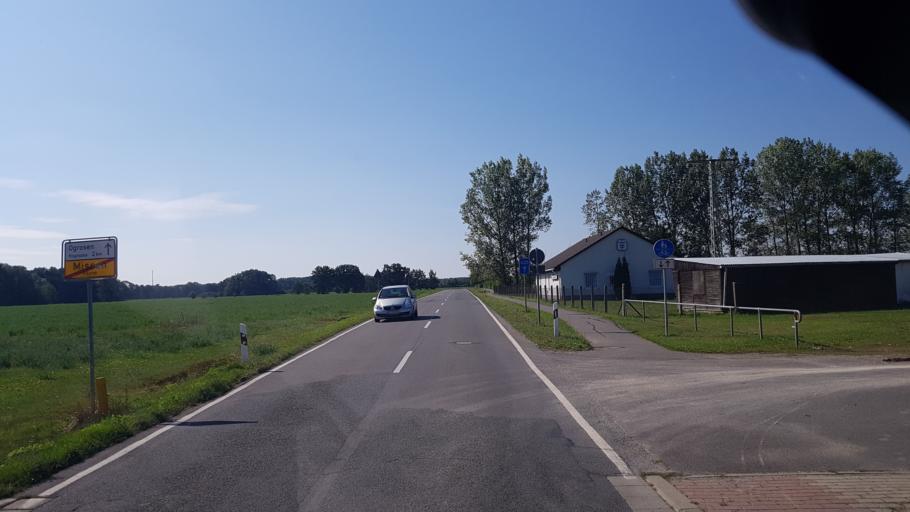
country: DE
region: Brandenburg
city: Vetschau
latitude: 51.7264
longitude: 14.0451
